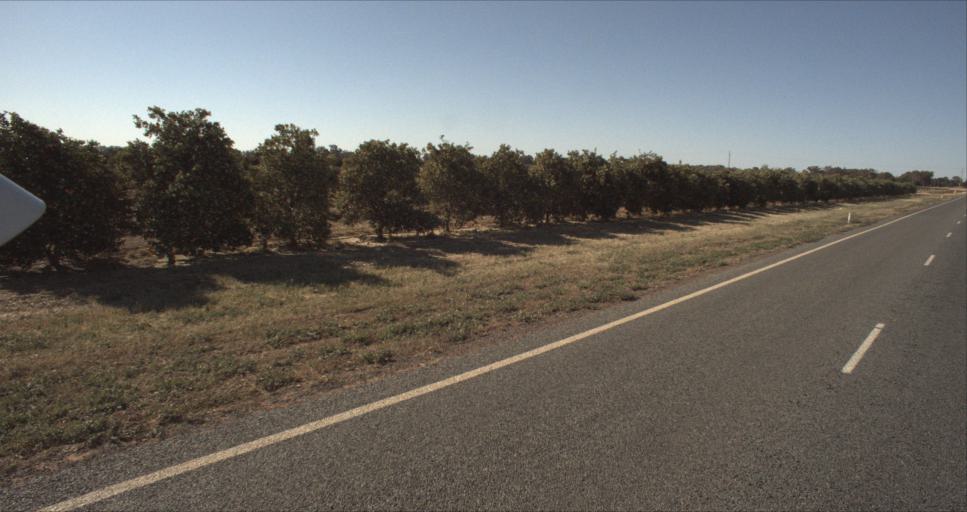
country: AU
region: New South Wales
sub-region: Leeton
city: Leeton
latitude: -34.6169
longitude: 146.4001
